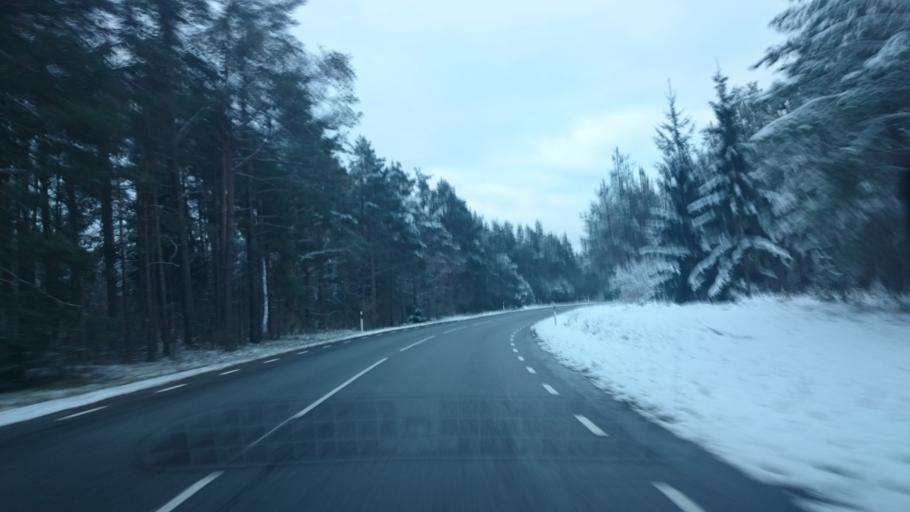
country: EE
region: Saare
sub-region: Kuressaare linn
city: Kuressaare
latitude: 58.3898
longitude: 22.6487
